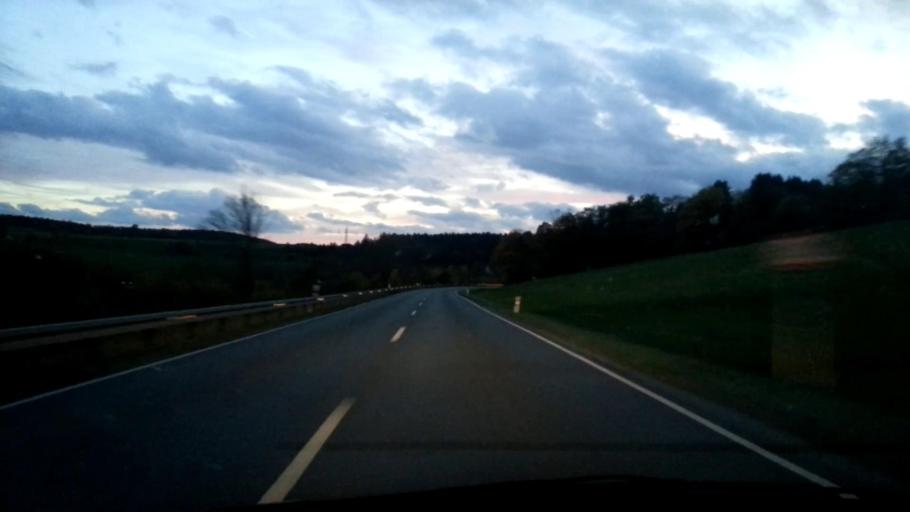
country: DE
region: Bavaria
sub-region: Upper Franconia
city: Neunkirchen am Main
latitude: 49.9603
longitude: 11.6522
